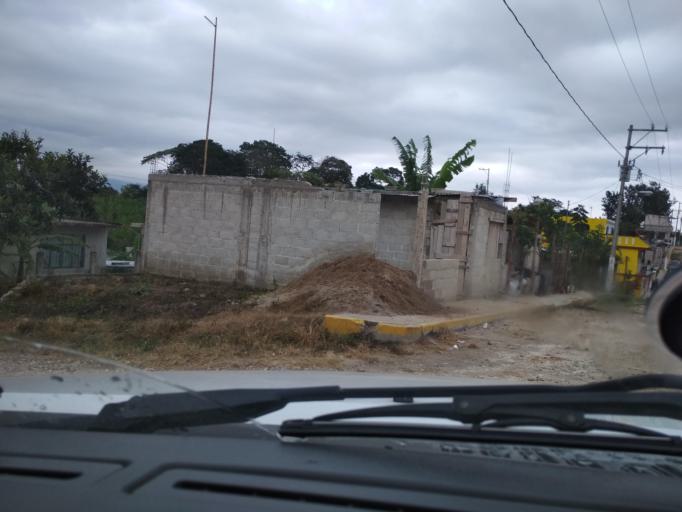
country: MX
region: Veracruz
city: El Castillo
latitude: 19.5724
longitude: -96.8523
